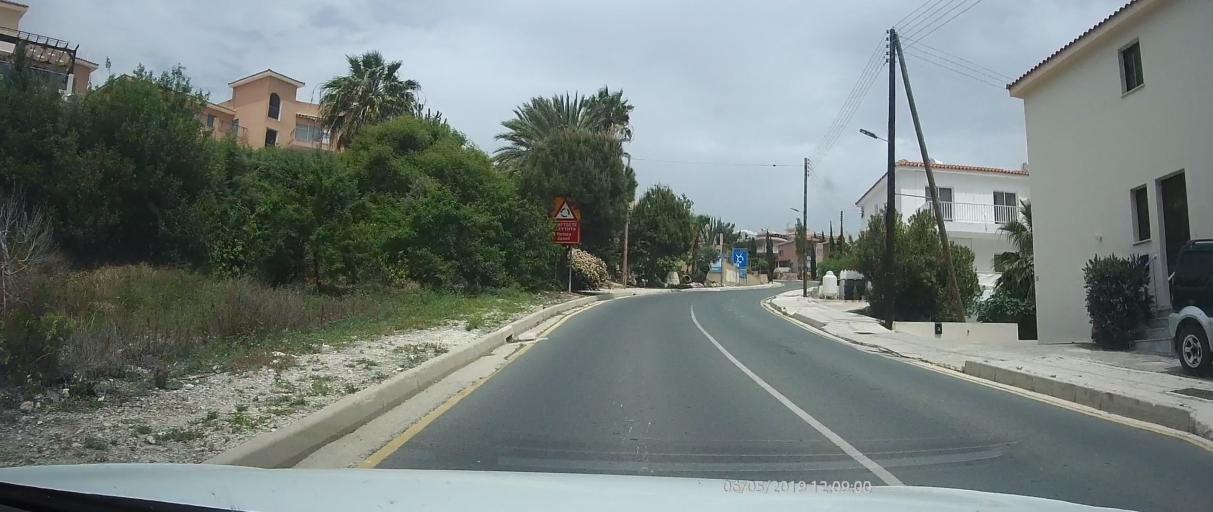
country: CY
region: Pafos
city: Tala
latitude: 34.8374
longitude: 32.4334
